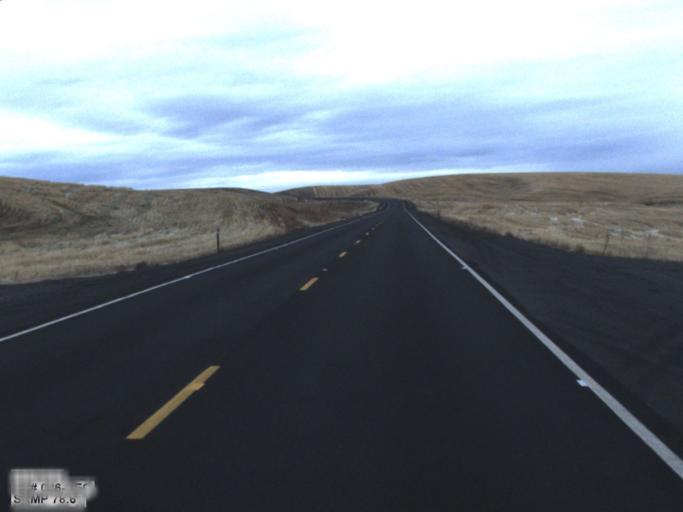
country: US
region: Washington
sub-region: Adams County
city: Ritzville
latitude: 46.7865
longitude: -118.3851
